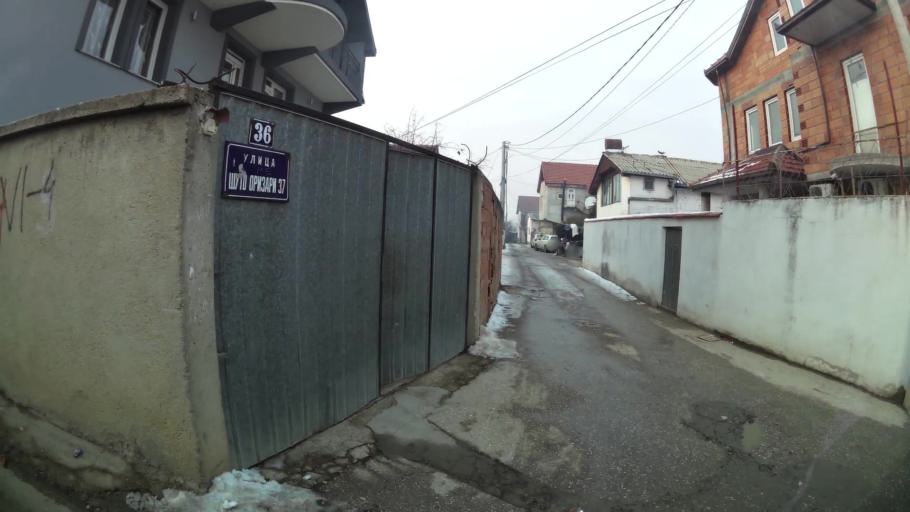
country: MK
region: Suto Orizari
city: Suto Orizare
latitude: 42.0327
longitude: 21.4204
